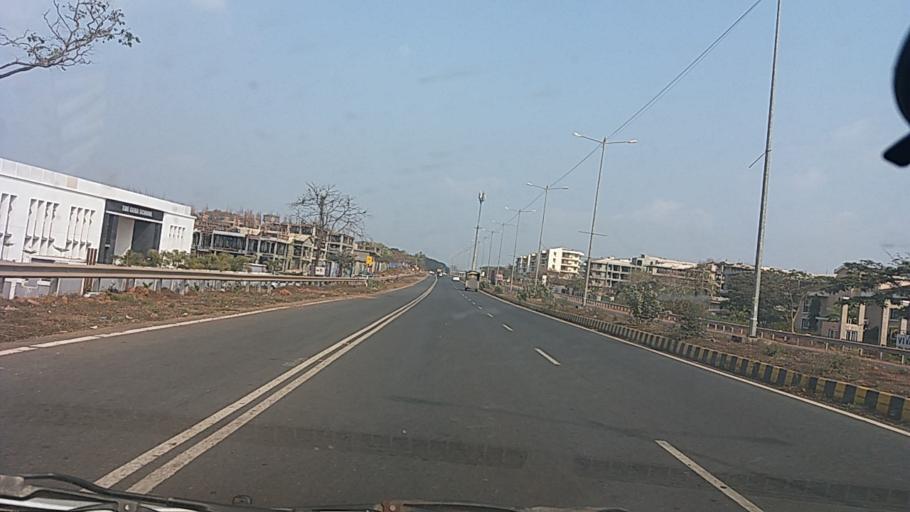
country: IN
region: Goa
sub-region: North Goa
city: Bambolim
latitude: 15.4914
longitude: 73.8898
